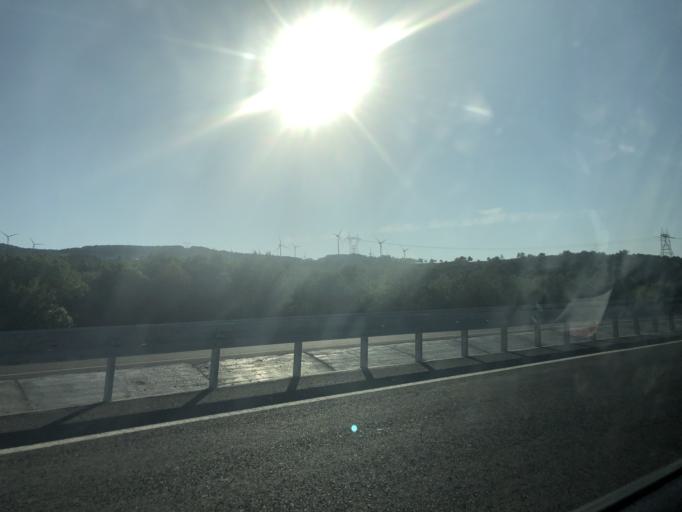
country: TR
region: Istanbul
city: Catalca
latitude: 41.1513
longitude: 28.4693
